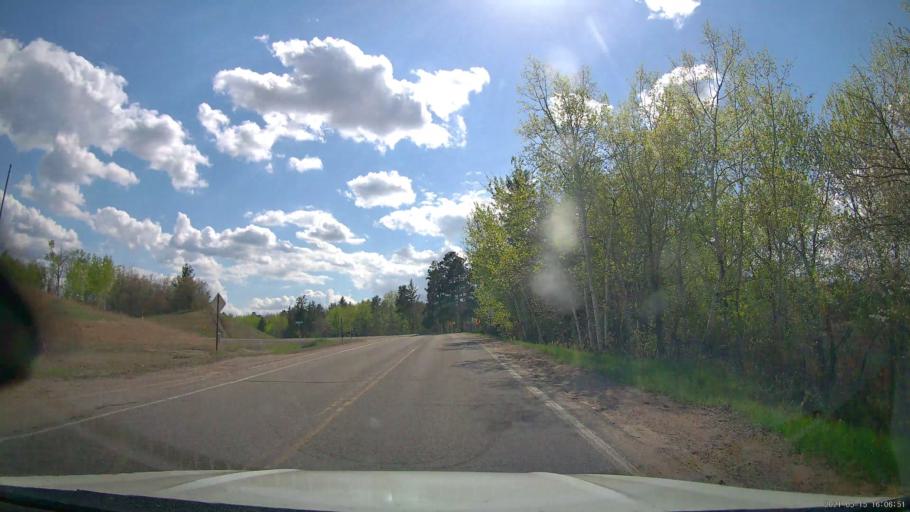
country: US
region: Minnesota
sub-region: Hubbard County
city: Park Rapids
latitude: 46.9775
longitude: -94.9518
